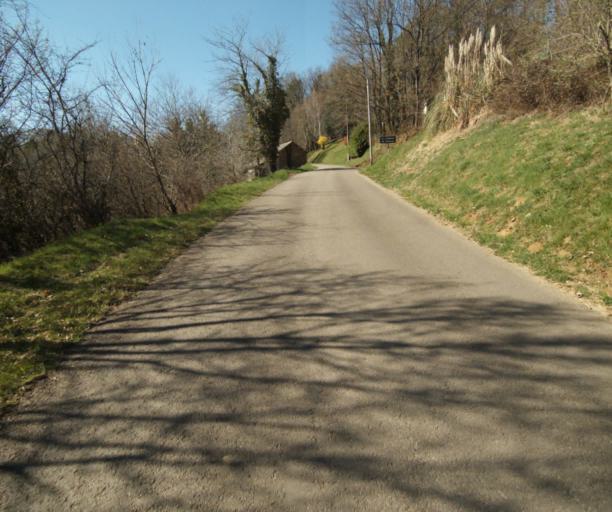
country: FR
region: Limousin
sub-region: Departement de la Correze
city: Tulle
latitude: 45.2722
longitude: 1.7302
